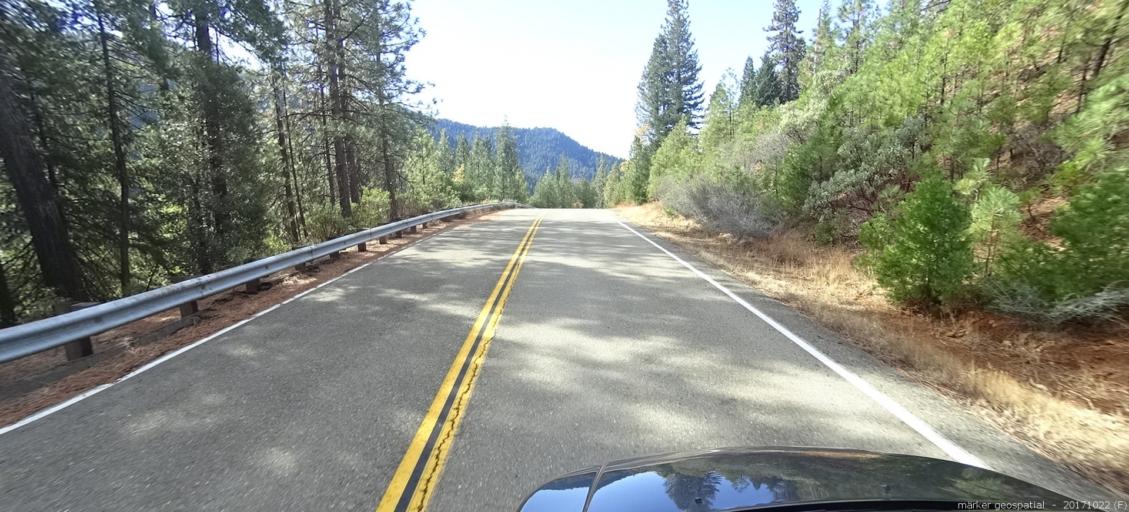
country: US
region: California
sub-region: Siskiyou County
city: Dunsmuir
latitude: 41.0638
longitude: -122.3704
